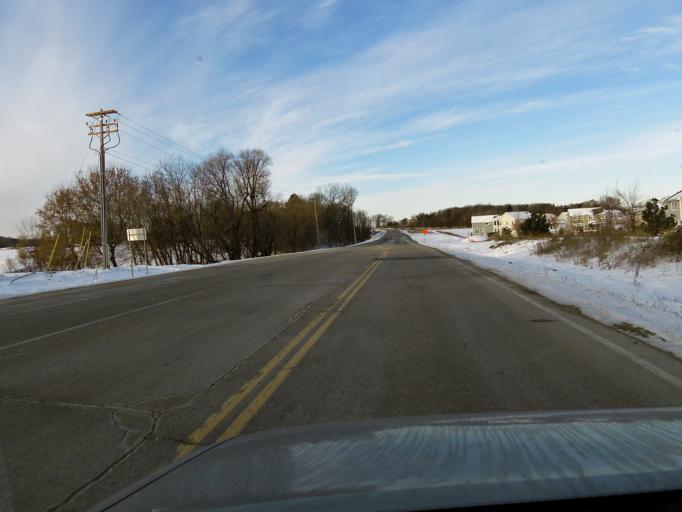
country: US
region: Minnesota
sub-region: Scott County
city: Prior Lake
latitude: 44.7655
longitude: -93.4207
